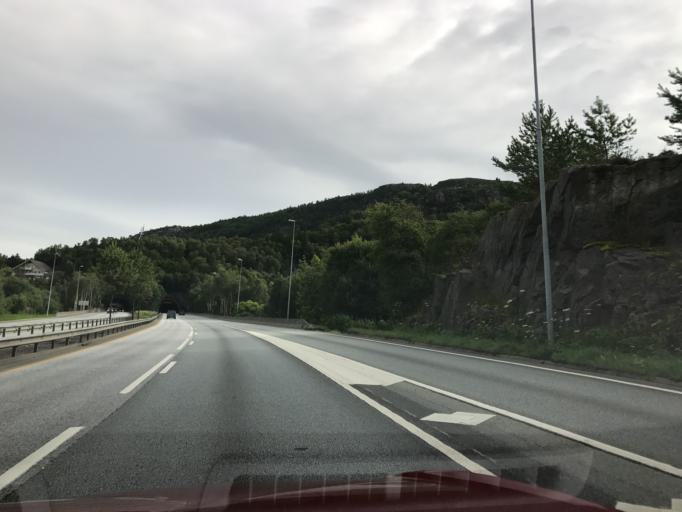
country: NO
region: Hordaland
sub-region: Bergen
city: Bergen
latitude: 60.4379
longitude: 5.3238
